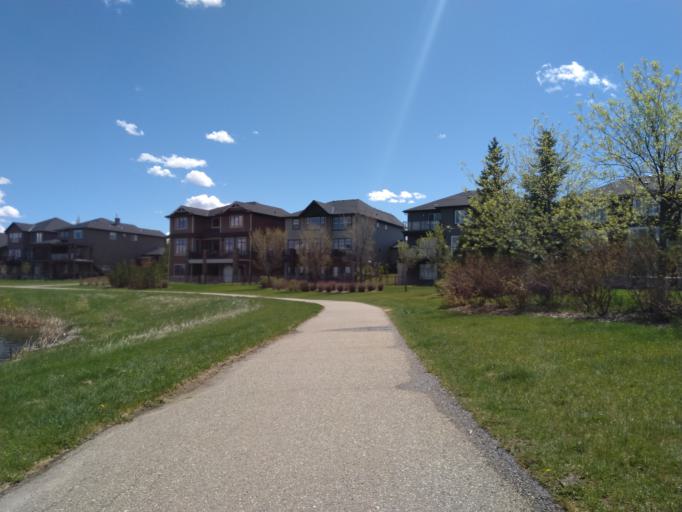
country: CA
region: Alberta
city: Chestermere
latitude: 51.0207
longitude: -113.8358
